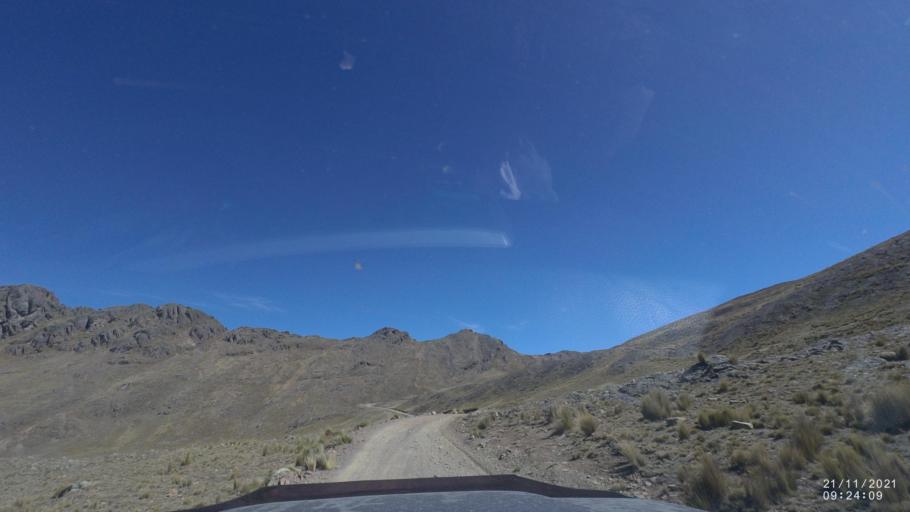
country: BO
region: Cochabamba
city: Cochabamba
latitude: -17.0936
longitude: -66.2547
